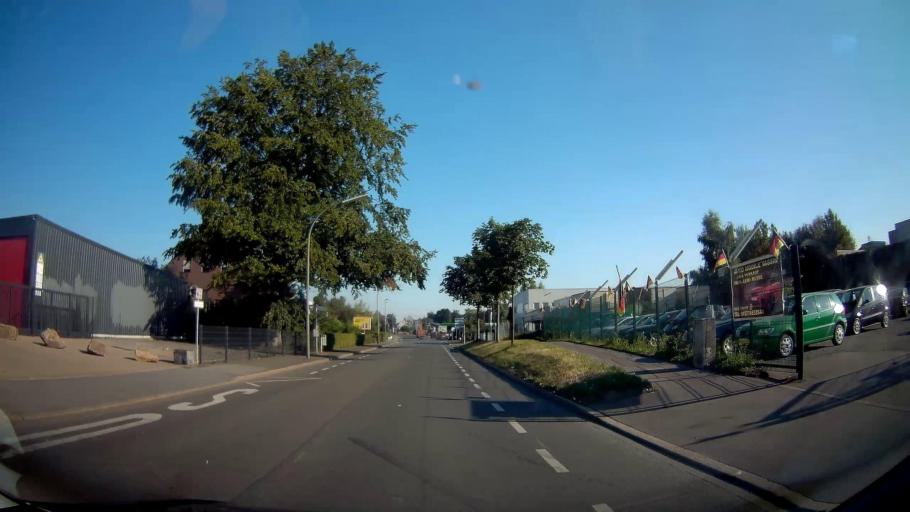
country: DE
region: North Rhine-Westphalia
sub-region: Regierungsbezirk Arnsberg
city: Dortmund
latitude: 51.5440
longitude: 7.4512
